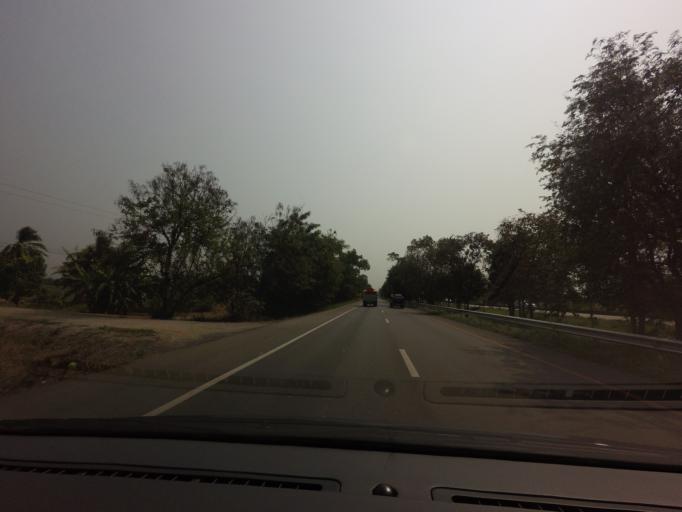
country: TH
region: Prachuap Khiri Khan
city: Hua Hin
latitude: 12.4913
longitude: 99.8898
